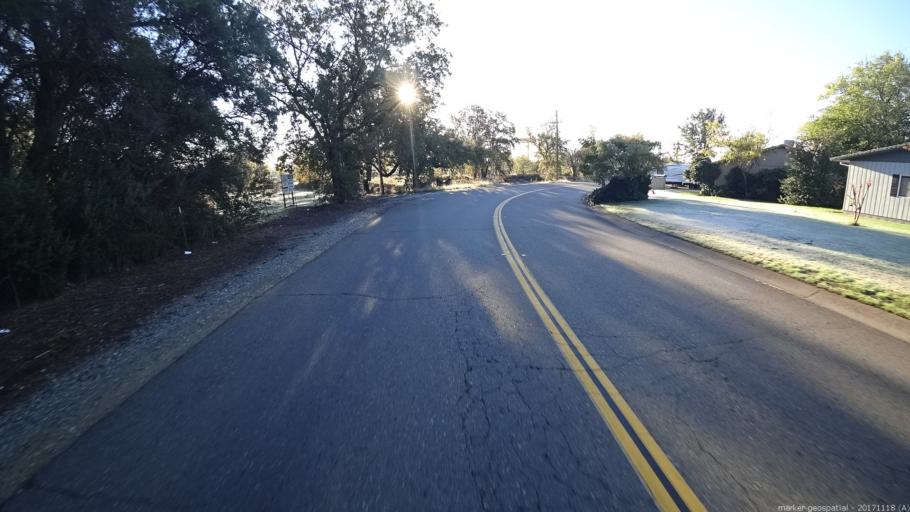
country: US
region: California
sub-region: Shasta County
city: Cottonwood
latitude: 40.3911
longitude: -122.2882
